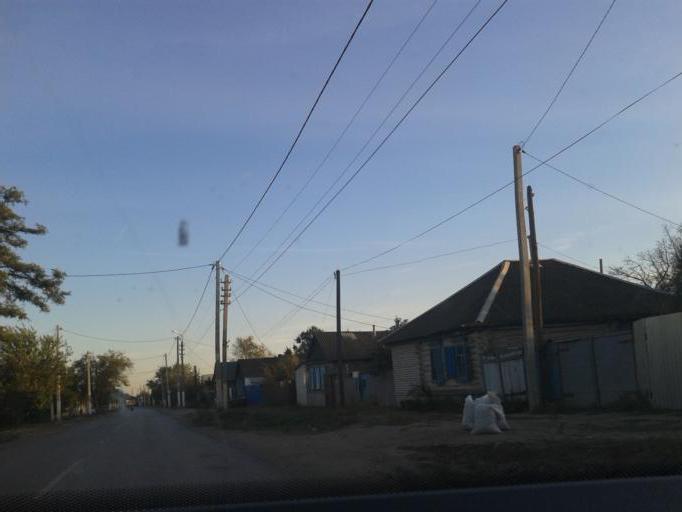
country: RU
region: Volgograd
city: Krasnoslobodsk
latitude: 48.7066
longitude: 44.5649
